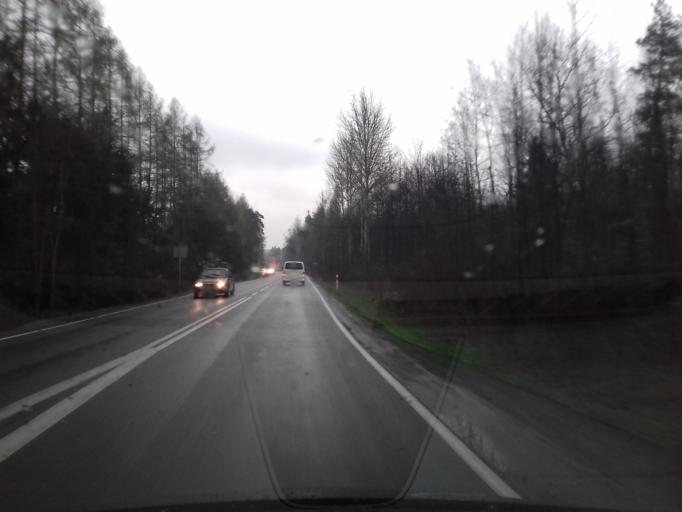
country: PL
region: Lesser Poland Voivodeship
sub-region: Powiat nowosadecki
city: Stary Sacz
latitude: 49.5622
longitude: 20.6561
